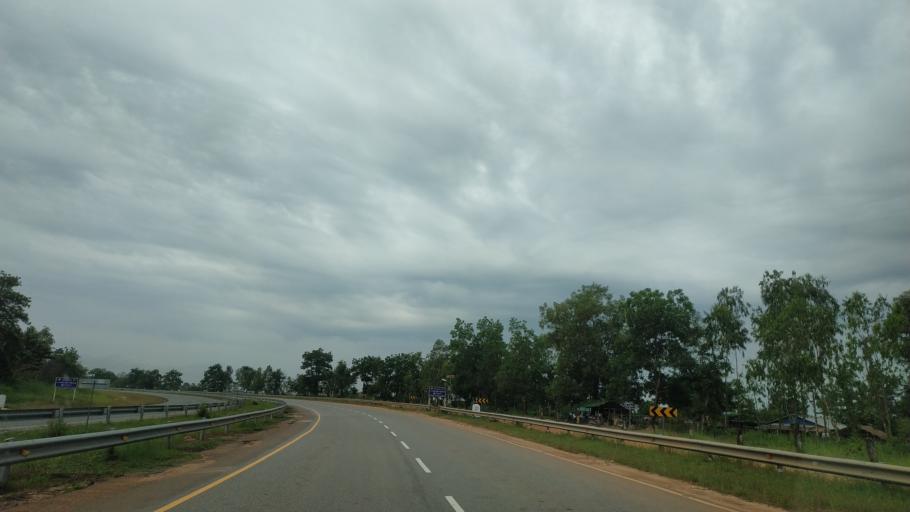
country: MM
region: Bago
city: Thanatpin
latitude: 17.3373
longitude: 96.2139
